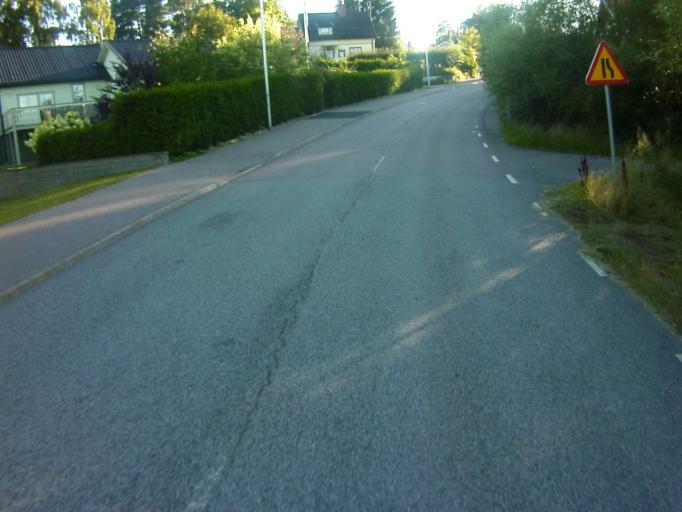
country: SE
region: Soedermanland
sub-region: Eskilstuna Kommun
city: Hallbybrunn
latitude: 59.3922
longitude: 16.4321
